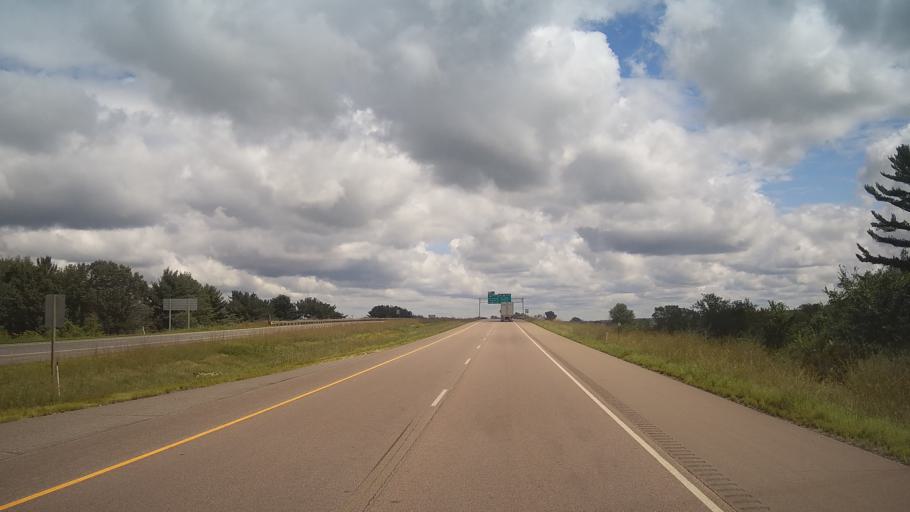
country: US
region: Wisconsin
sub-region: Monroe County
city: Tomah
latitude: 43.9764
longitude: -90.4644
